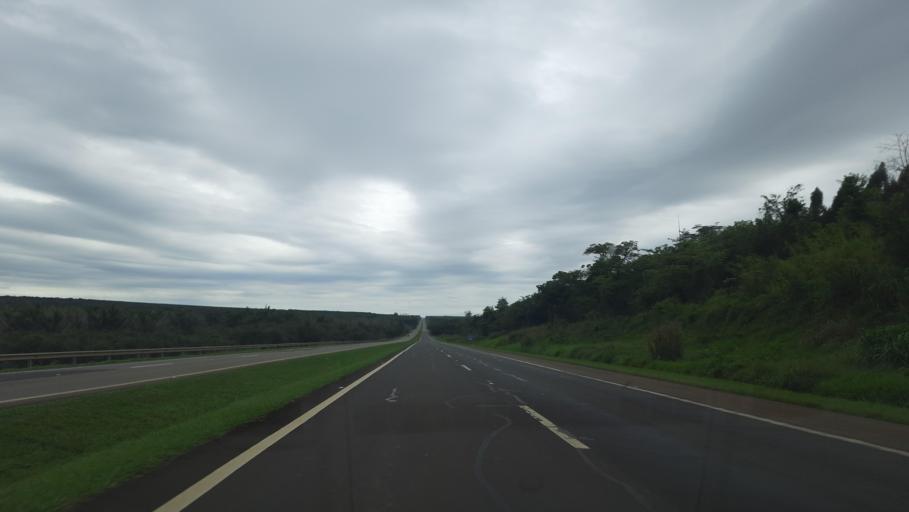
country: BR
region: Sao Paulo
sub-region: Casa Branca
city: Casa Branca
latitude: -21.8390
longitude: -47.0664
